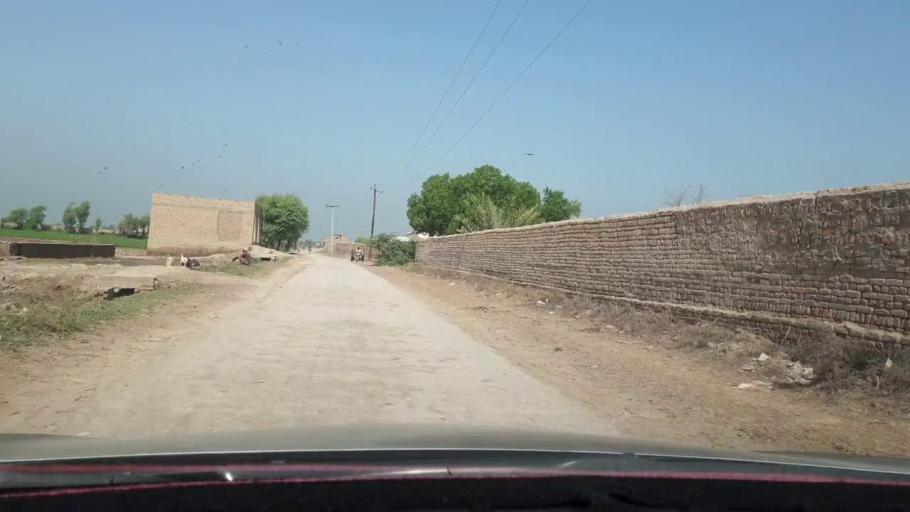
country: PK
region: Sindh
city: Kambar
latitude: 27.5969
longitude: 67.9883
